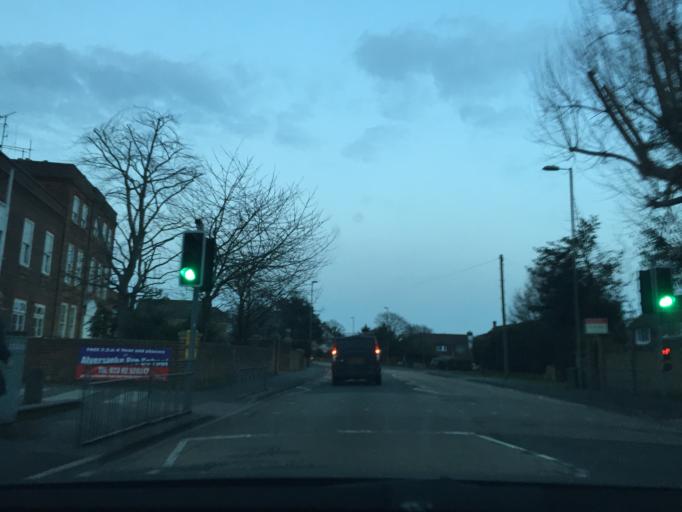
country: GB
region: England
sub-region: Hampshire
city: Gosport
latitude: 50.7925
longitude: -1.1473
